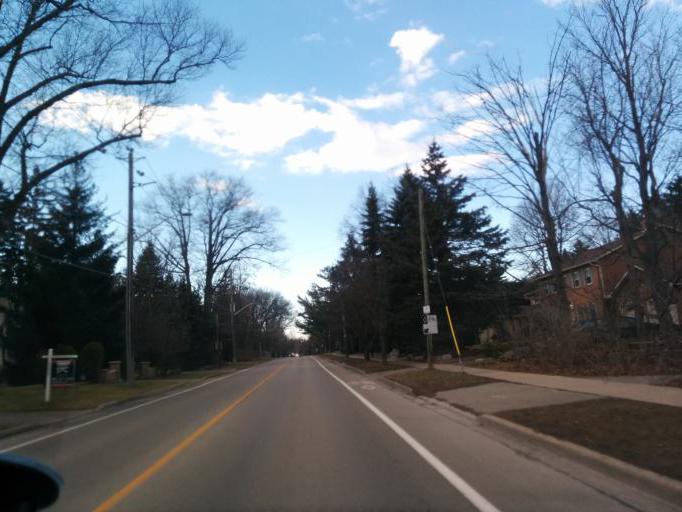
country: CA
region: Ontario
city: Mississauga
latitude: 43.5338
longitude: -79.6250
